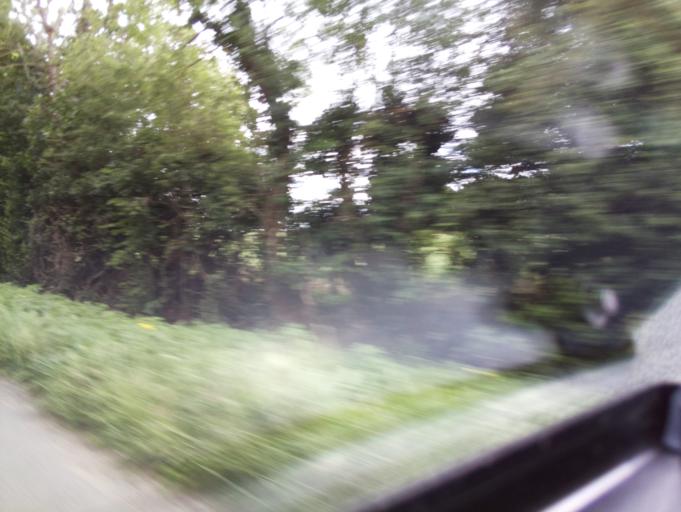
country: GB
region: England
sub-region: Nottinghamshire
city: Cotgrave
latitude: 52.8448
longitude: -1.0662
